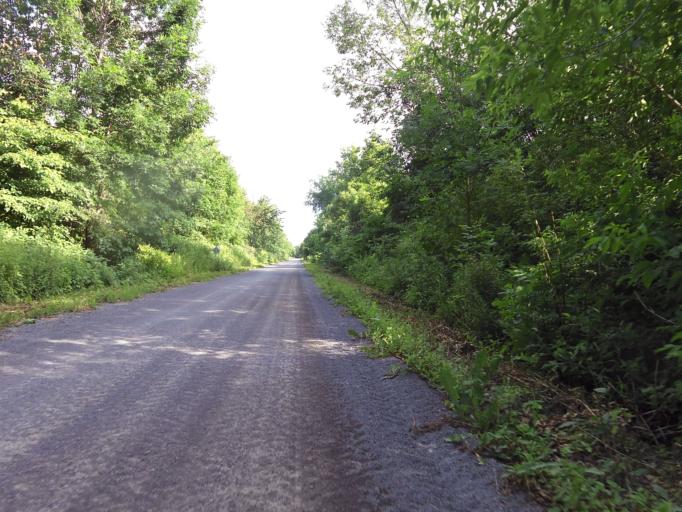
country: CA
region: Ontario
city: Arnprior
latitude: 45.3217
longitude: -76.2868
